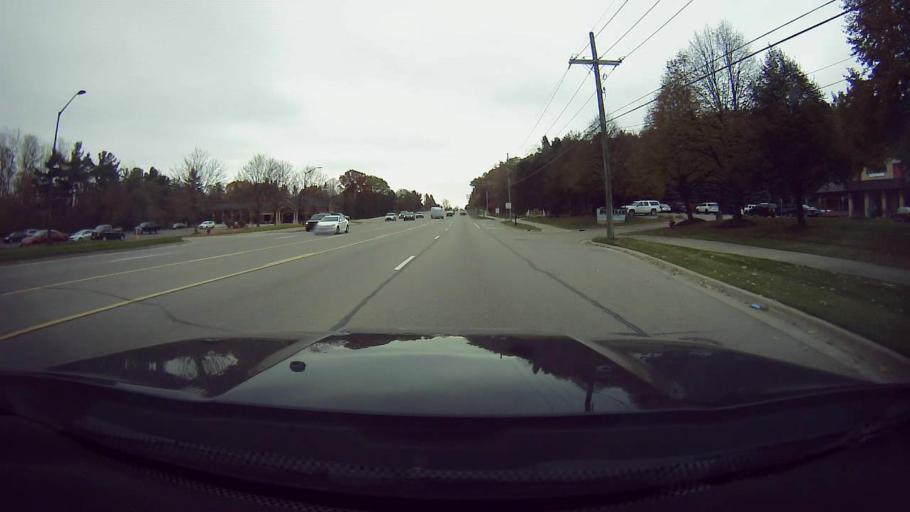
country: US
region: Michigan
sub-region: Oakland County
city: Waterford
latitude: 42.7131
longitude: -83.4102
